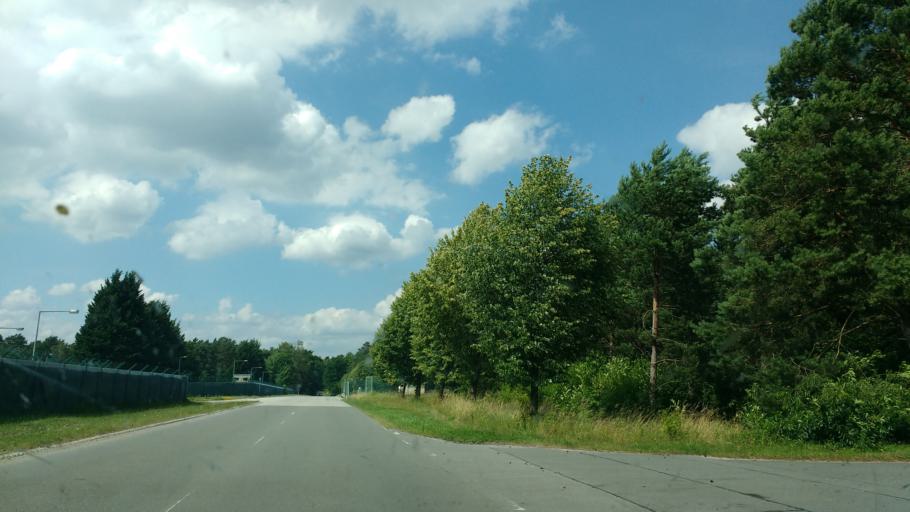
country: DE
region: North Rhine-Westphalia
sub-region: Regierungsbezirk Detmold
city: Paderborn
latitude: 51.7702
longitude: 8.7565
